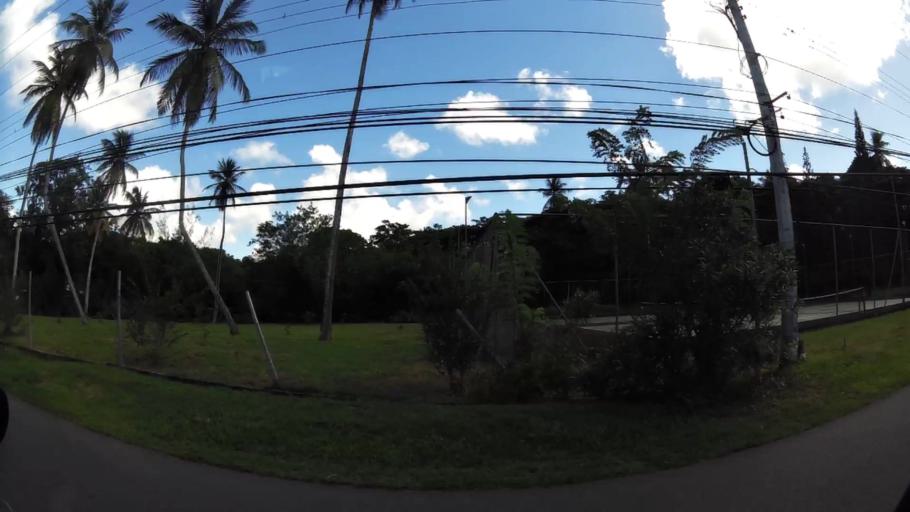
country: TT
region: Tobago
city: Scarborough
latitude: 11.2138
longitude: -60.7773
